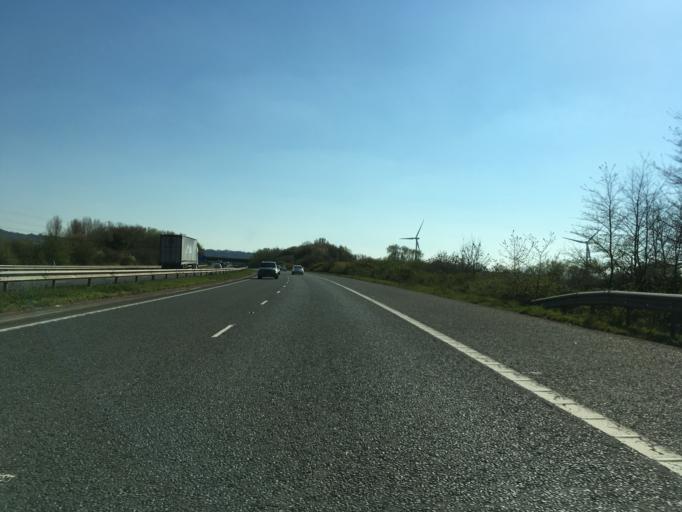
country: GB
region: England
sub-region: South Gloucestershire
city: Severn Beach
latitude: 51.5222
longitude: -2.6593
